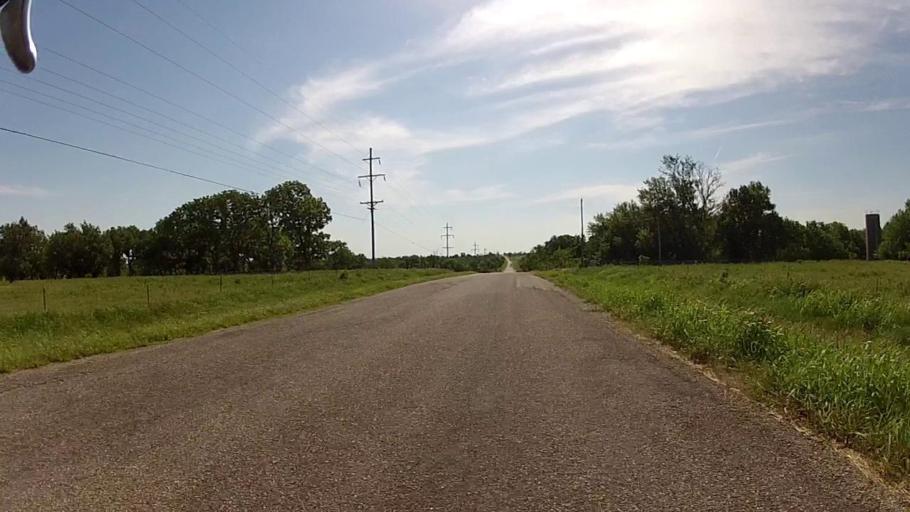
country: US
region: Kansas
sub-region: Cowley County
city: Winfield
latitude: 37.0710
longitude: -96.6690
